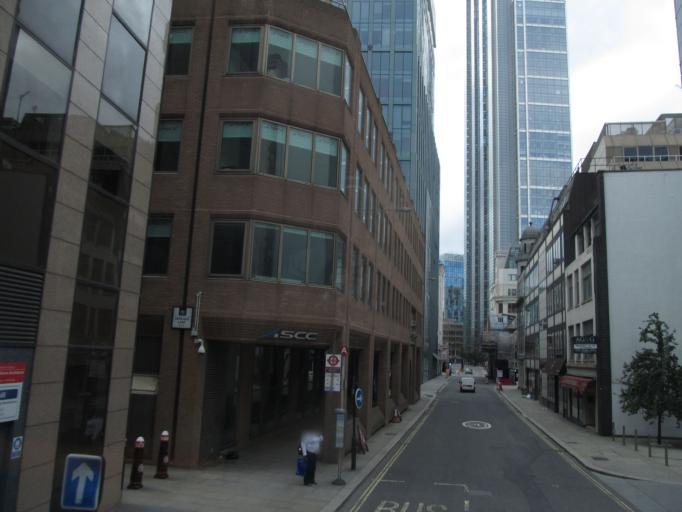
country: GB
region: England
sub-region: Greater London
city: City of London
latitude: 51.5145
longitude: -0.0783
